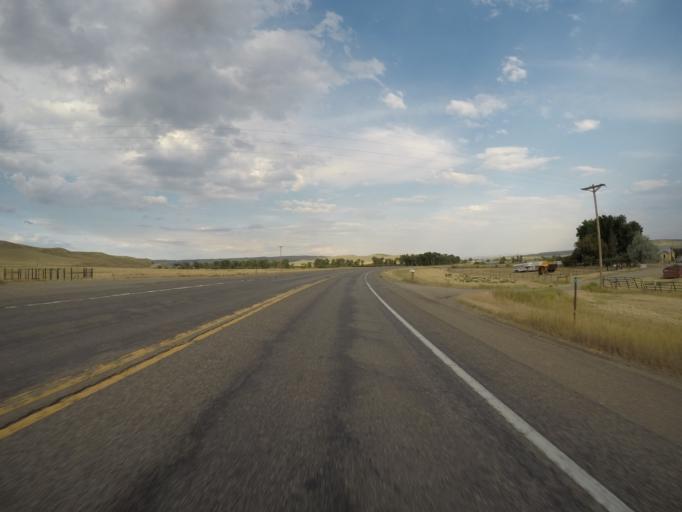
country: US
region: Colorado
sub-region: Moffat County
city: Craig
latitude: 40.5336
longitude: -107.4410
